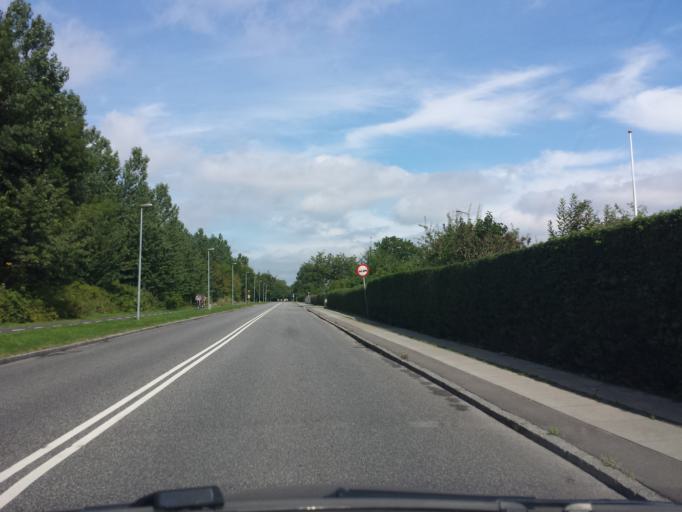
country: DK
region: Capital Region
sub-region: Ballerup Kommune
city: Ballerup
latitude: 55.7163
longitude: 12.3885
